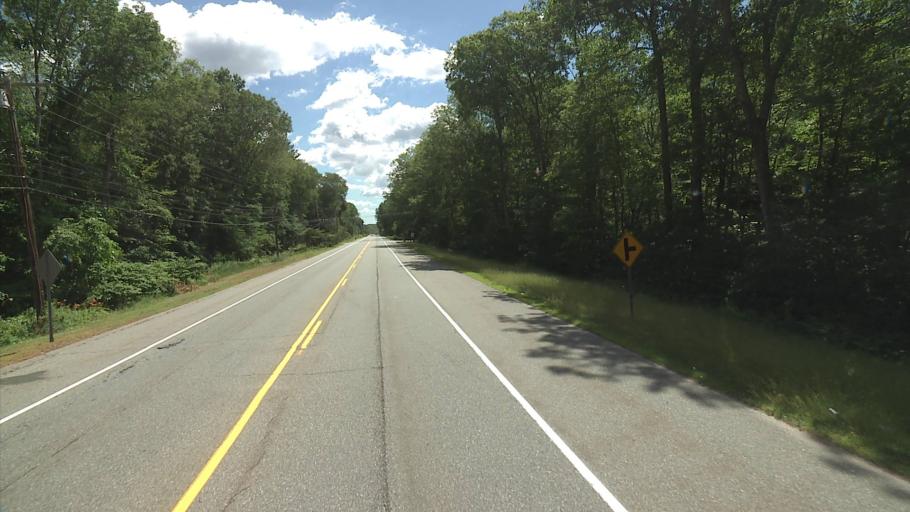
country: US
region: Connecticut
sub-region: New London County
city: Old Mystic
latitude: 41.3896
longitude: -71.9967
